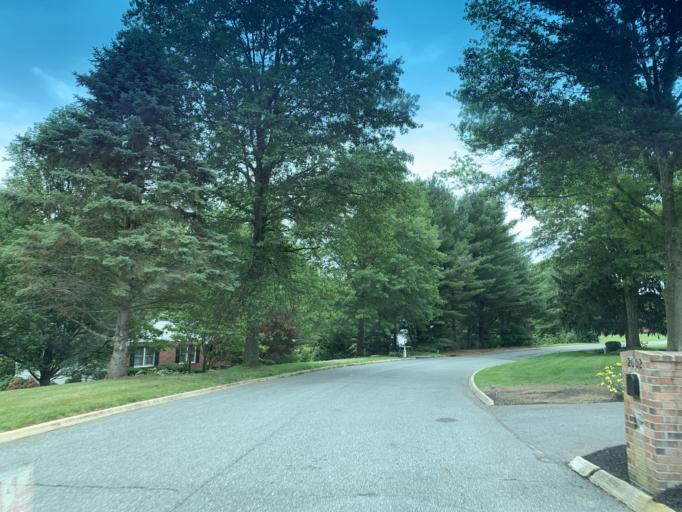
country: US
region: Maryland
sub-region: Harford County
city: Fallston
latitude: 39.5433
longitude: -76.4315
